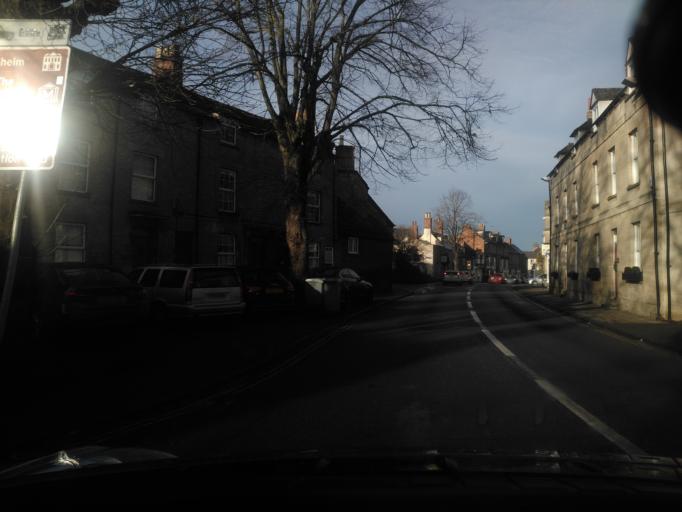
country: GB
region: England
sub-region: Oxfordshire
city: Woodstock
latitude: 51.8466
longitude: -1.3528
